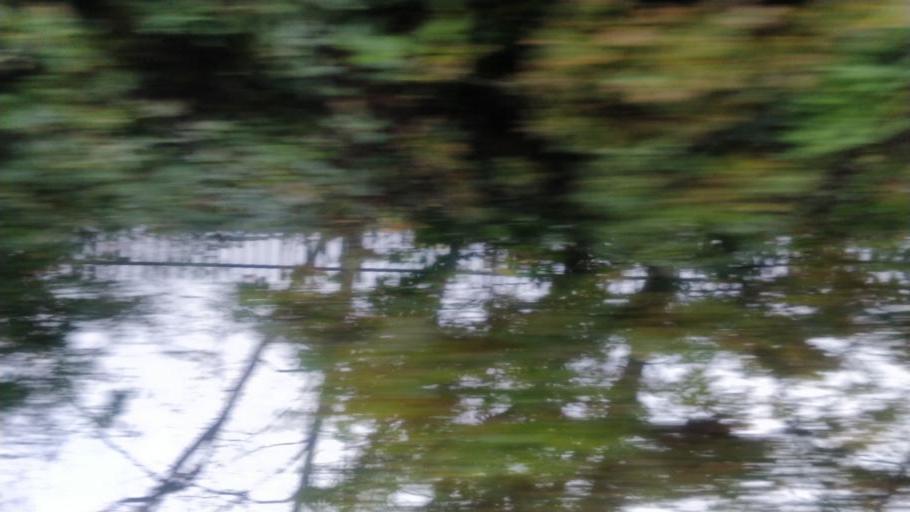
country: GB
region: England
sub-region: Borough of Wigan
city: Shevington
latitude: 53.5589
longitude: -2.6897
